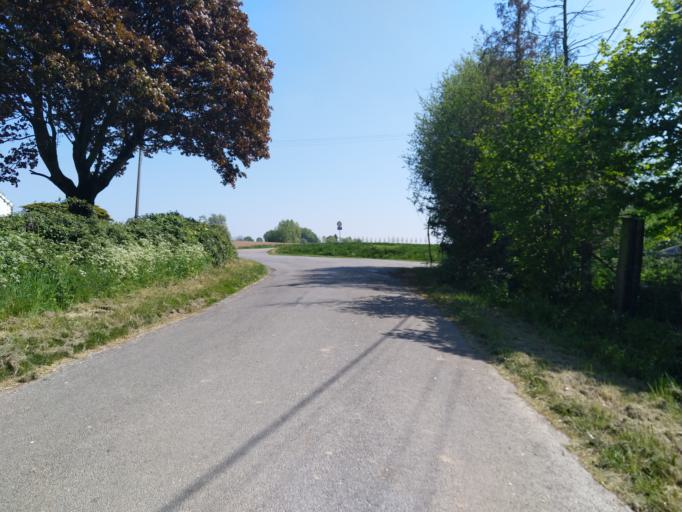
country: BE
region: Wallonia
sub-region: Province du Hainaut
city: Braine-le-Comte
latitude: 50.6090
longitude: 4.1048
